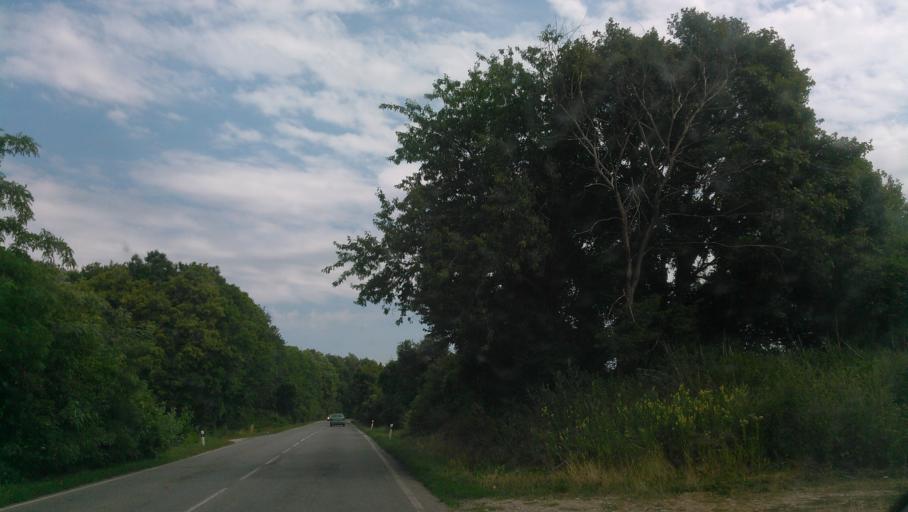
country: SK
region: Trnavsky
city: Hlohovec
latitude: 48.4409
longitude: 17.8336
